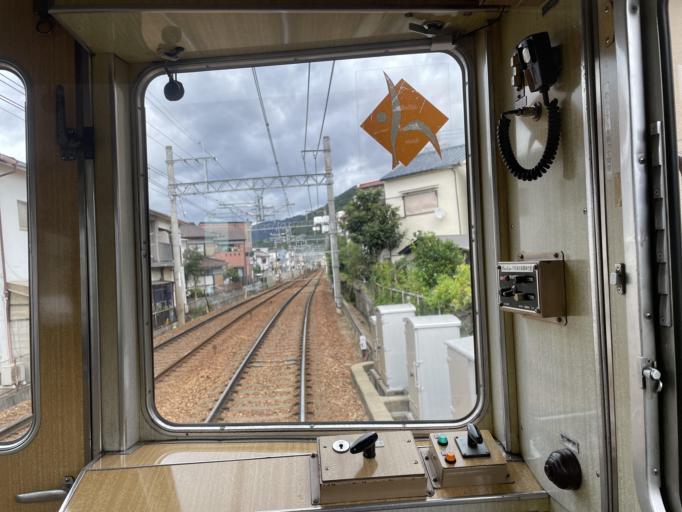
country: JP
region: Osaka
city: Ikeda
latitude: 34.8313
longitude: 135.4190
